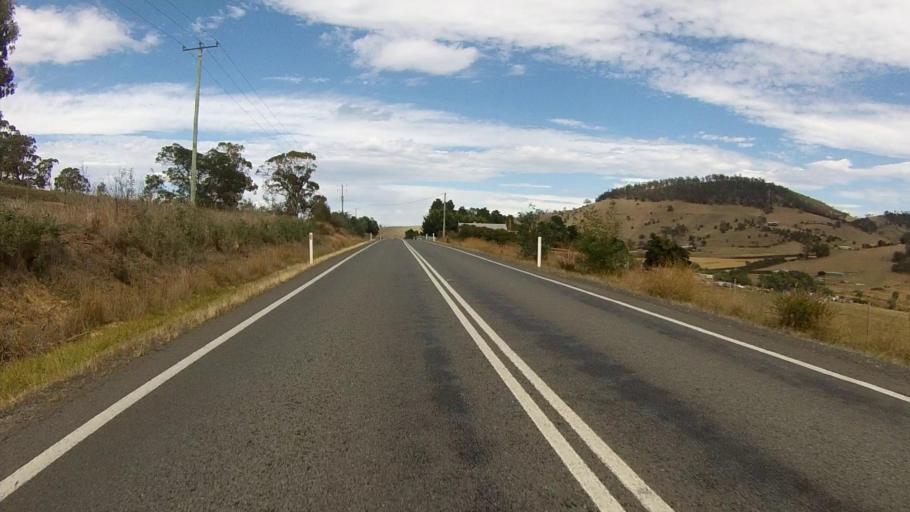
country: AU
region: Tasmania
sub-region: Brighton
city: Old Beach
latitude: -42.6690
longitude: 147.3699
